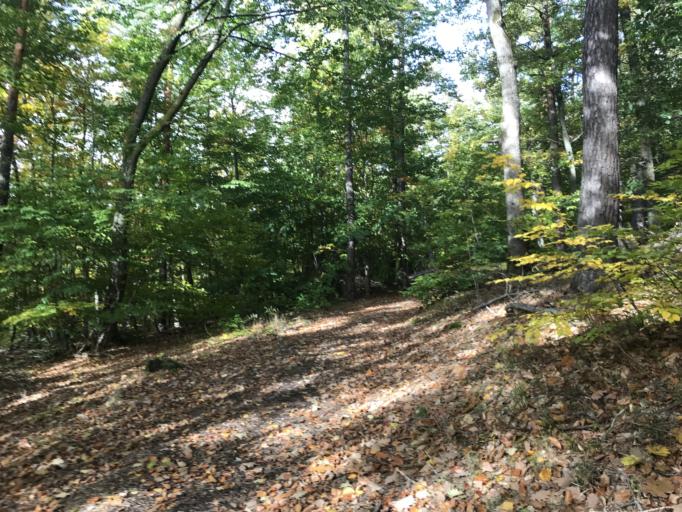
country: DE
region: Rheinland-Pfalz
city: Dannenfels
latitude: 49.6590
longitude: 7.9698
